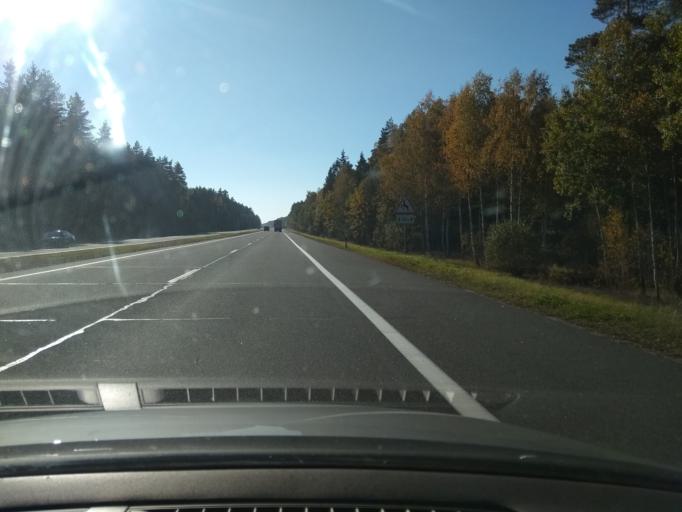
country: BY
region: Brest
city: Baranovichi
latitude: 53.0451
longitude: 25.8364
